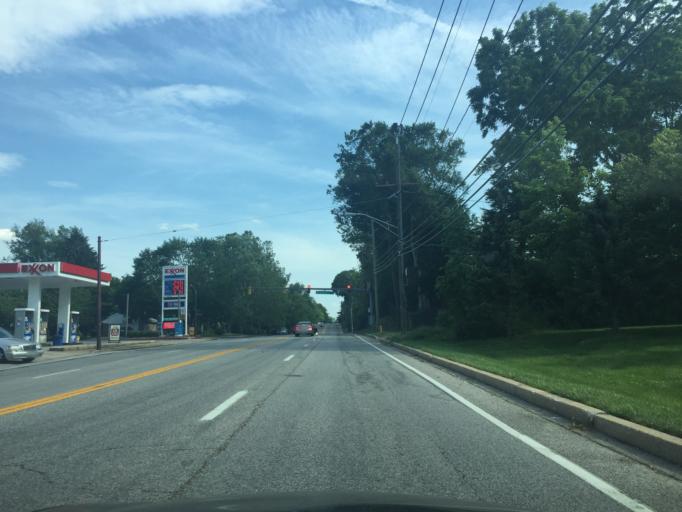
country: US
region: Maryland
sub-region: Baltimore County
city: Towson
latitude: 39.3777
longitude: -76.6270
